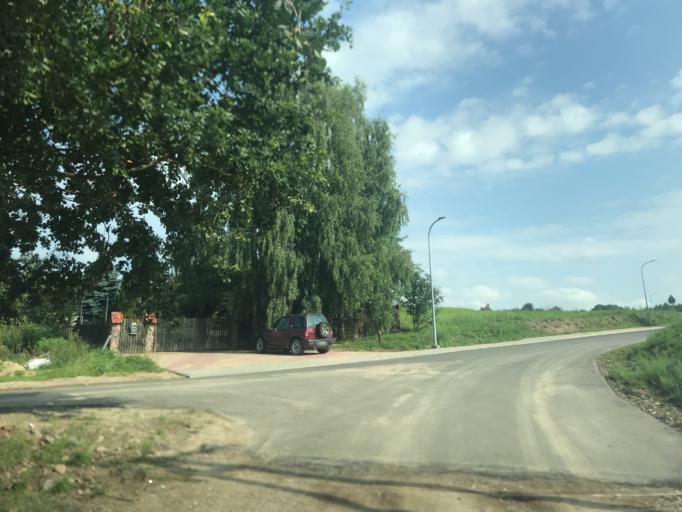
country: PL
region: Kujawsko-Pomorskie
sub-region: Powiat brodnicki
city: Brodnica
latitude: 53.3631
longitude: 19.4541
